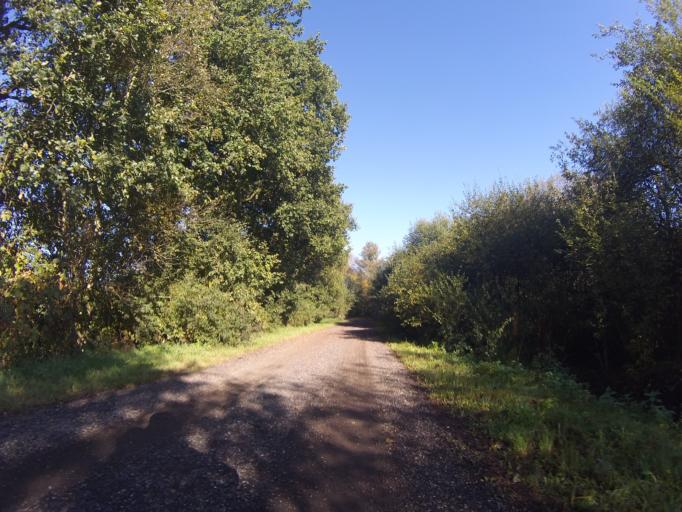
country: NL
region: Drenthe
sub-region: Gemeente Coevorden
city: Dalen
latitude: 52.7438
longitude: 6.6617
